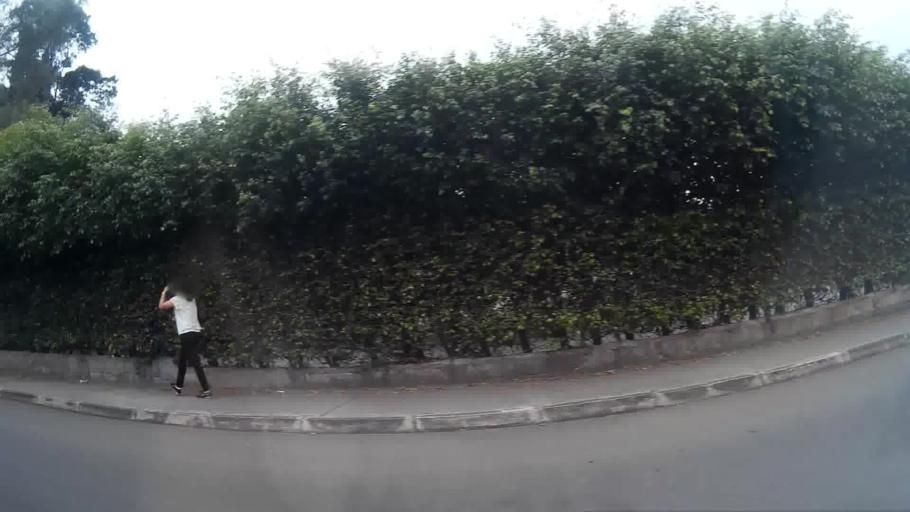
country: CO
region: Antioquia
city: Medellin
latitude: 6.2401
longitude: -75.5906
